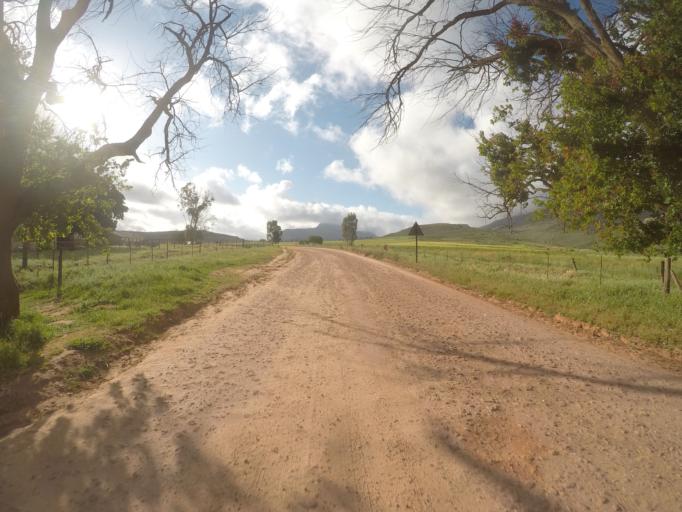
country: ZA
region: Western Cape
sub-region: West Coast District Municipality
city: Clanwilliam
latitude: -32.3432
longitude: 18.8342
